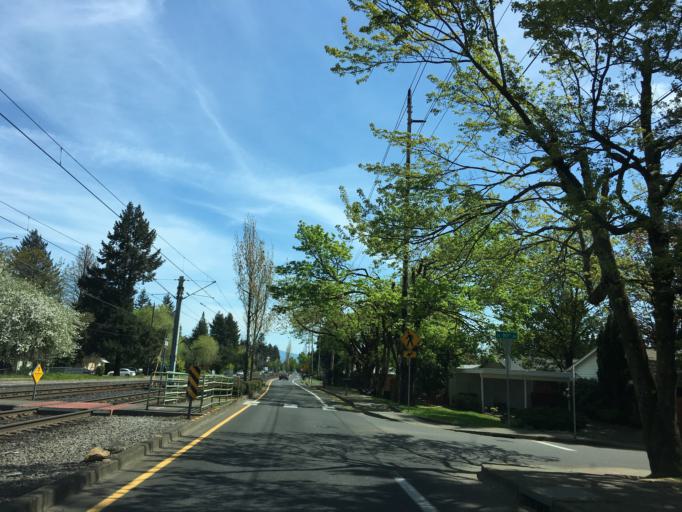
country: US
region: Oregon
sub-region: Multnomah County
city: Fairview
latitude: 45.5221
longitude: -122.4938
